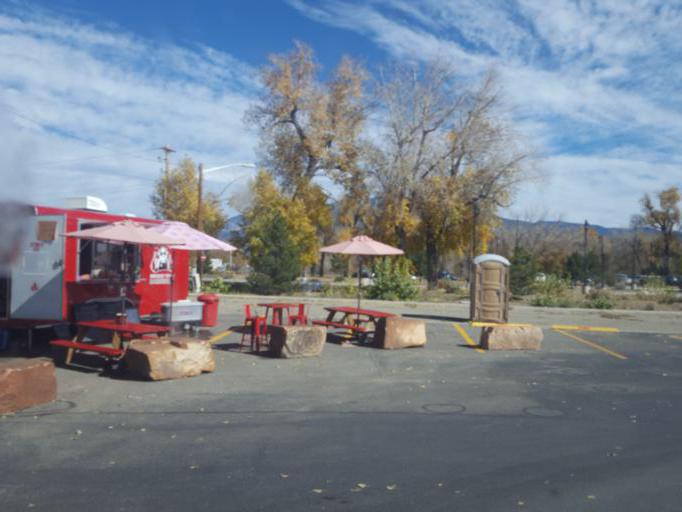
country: US
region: New Mexico
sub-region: Taos County
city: Taos
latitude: 36.3970
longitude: -105.5782
